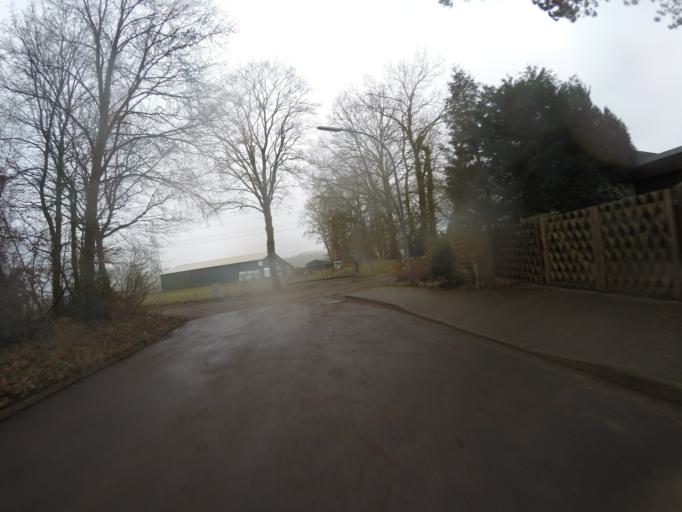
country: DE
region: Schleswig-Holstein
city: Quickborn
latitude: 53.7205
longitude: 9.9157
